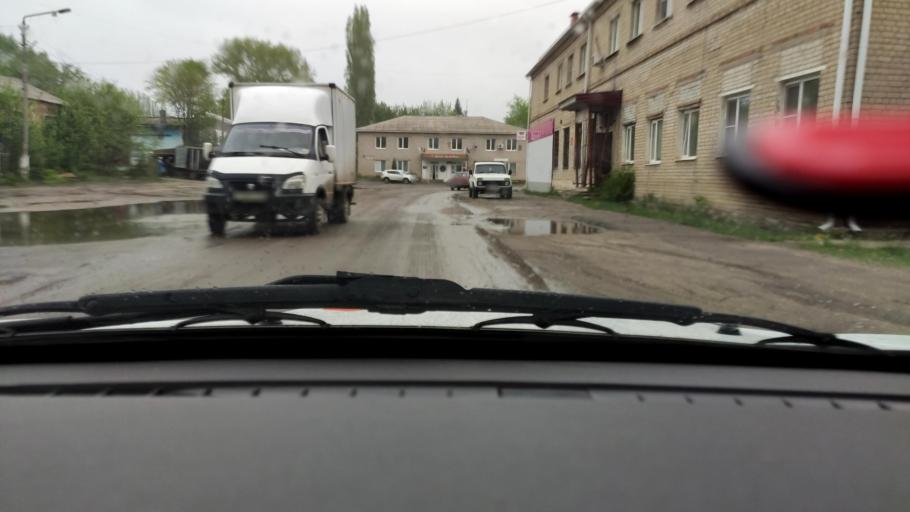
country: RU
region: Voronezj
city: Strelitsa
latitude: 51.6132
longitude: 38.8991
